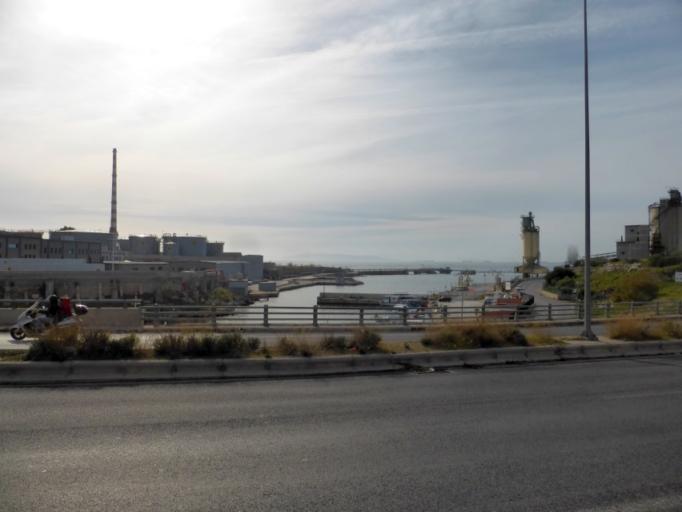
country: GR
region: Attica
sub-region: Nomos Piraios
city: Drapetsona
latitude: 37.9491
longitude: 23.6163
